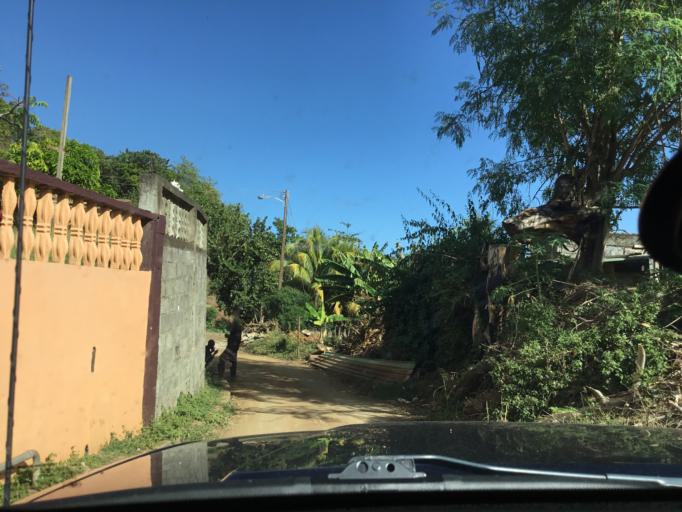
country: VC
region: Charlotte
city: Biabou
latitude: 13.1474
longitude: -61.1574
